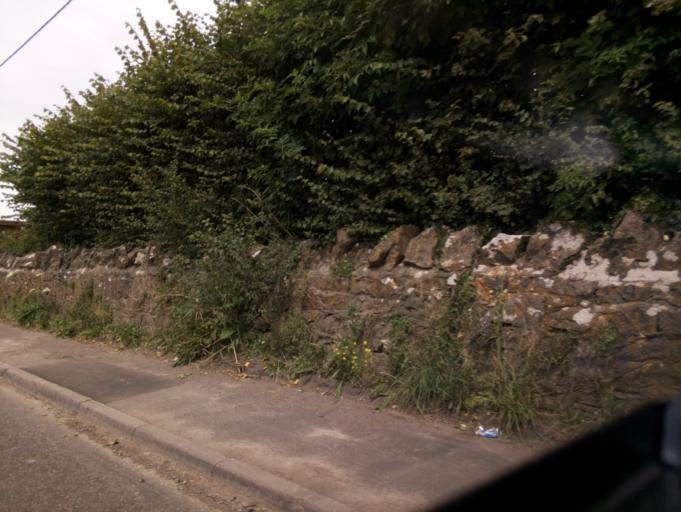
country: GB
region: England
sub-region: North Somerset
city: Kenn
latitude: 51.4005
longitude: -2.8400
